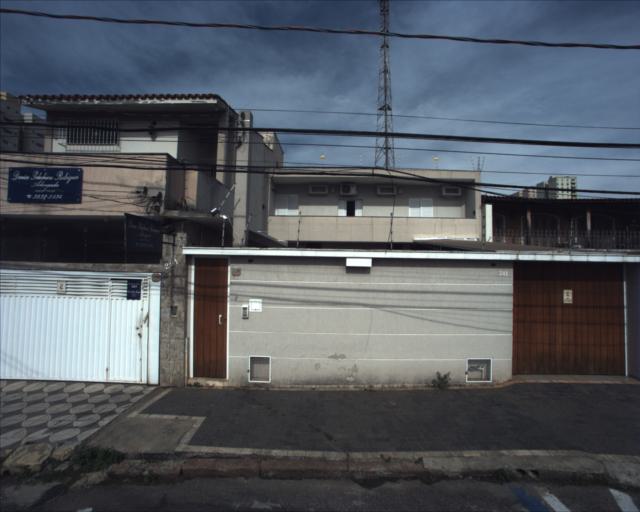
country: BR
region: Sao Paulo
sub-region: Sorocaba
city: Sorocaba
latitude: -23.4986
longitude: -47.4640
